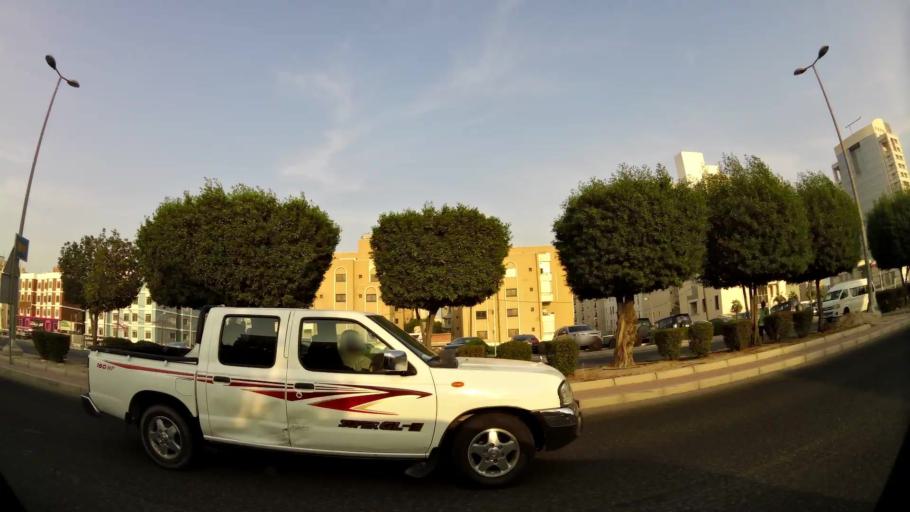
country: KW
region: Mubarak al Kabir
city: Sabah as Salim
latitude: 29.2510
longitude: 48.0803
